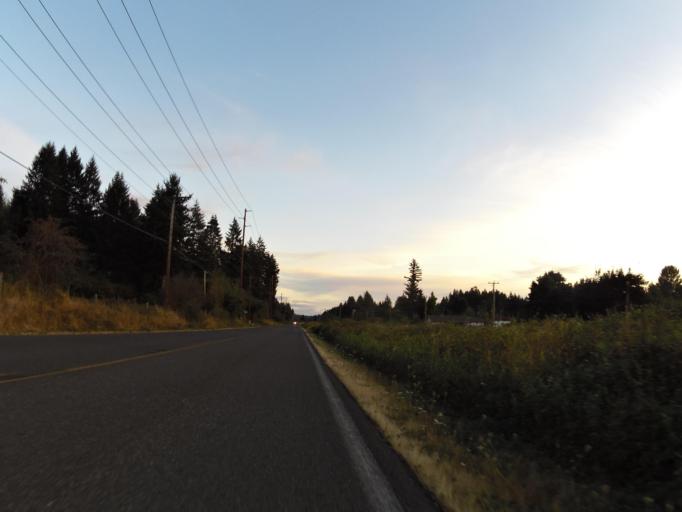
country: US
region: Washington
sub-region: Thurston County
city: Tenino
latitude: 46.8412
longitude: -122.8611
